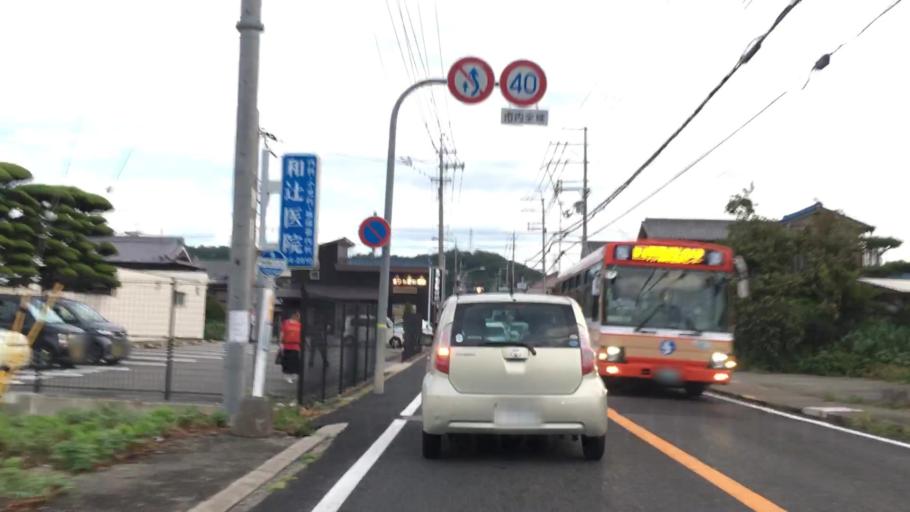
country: JP
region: Hyogo
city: Himeji
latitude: 34.8834
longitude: 134.7294
